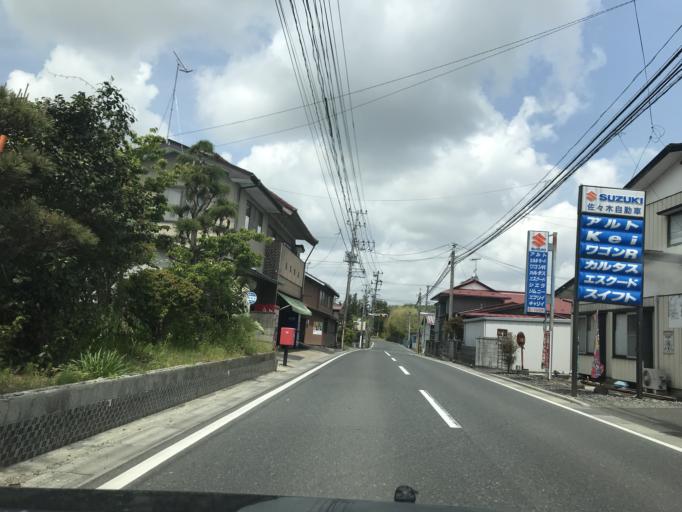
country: JP
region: Miyagi
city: Kogota
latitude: 38.6639
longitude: 141.0658
